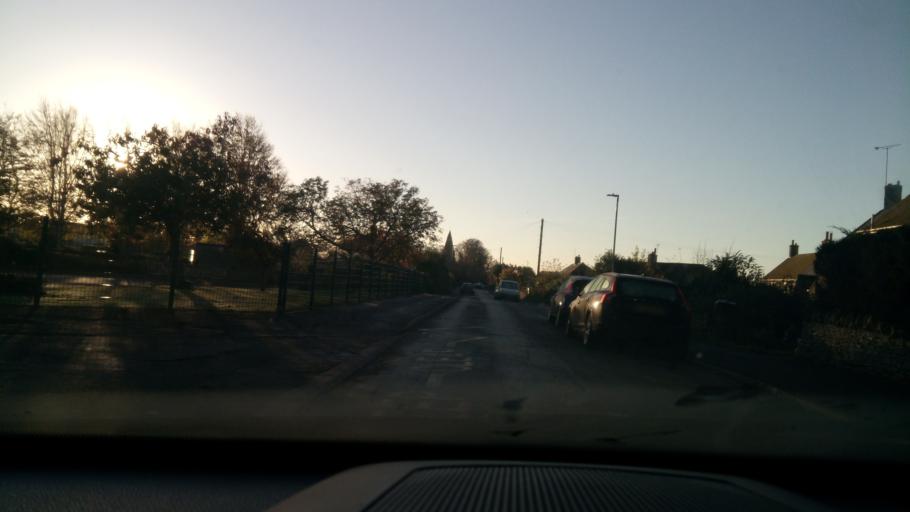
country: GB
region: England
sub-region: Peterborough
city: Wittering
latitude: 52.6082
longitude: -0.4442
